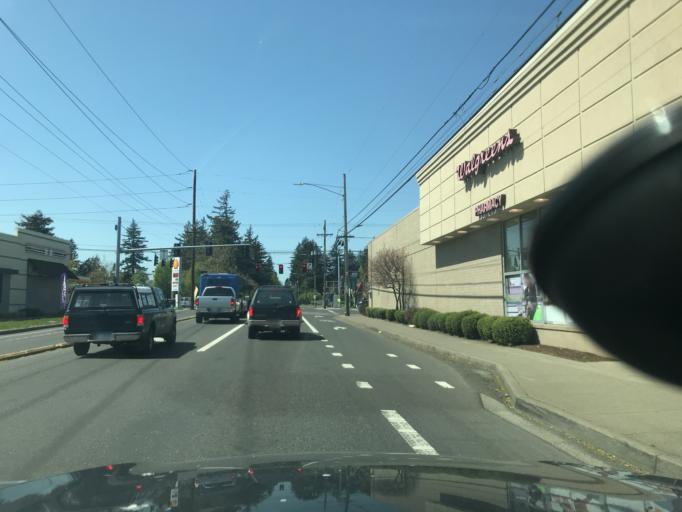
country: US
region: Oregon
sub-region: Multnomah County
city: Lents
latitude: 45.4971
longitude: -122.5369
